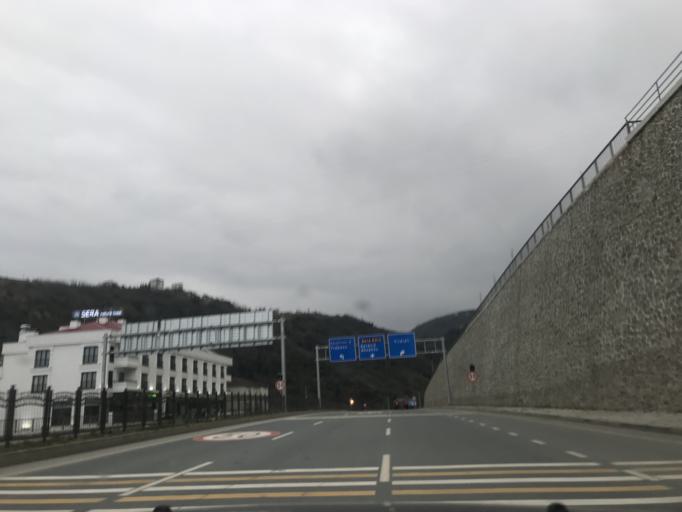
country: TR
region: Trabzon
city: Akcaabat
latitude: 41.0026
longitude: 39.6269
